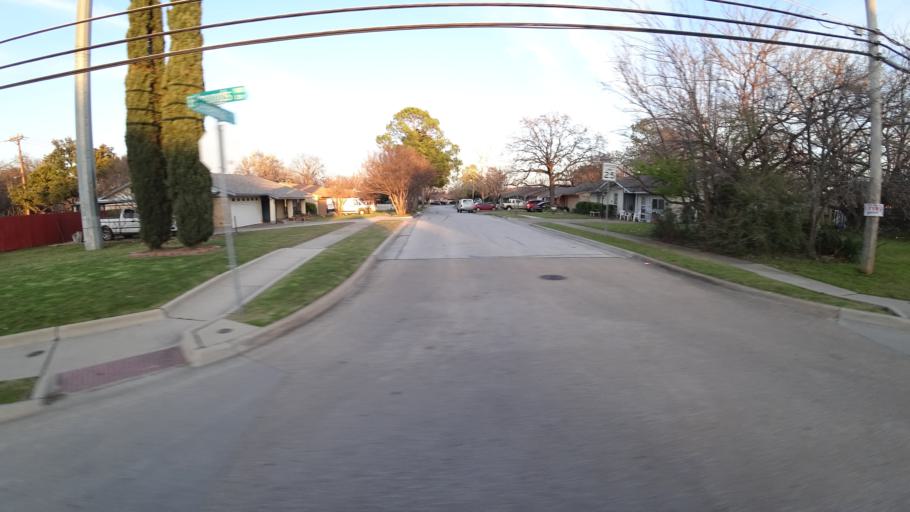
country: US
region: Texas
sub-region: Denton County
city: Lewisville
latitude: 33.0372
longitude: -97.0103
